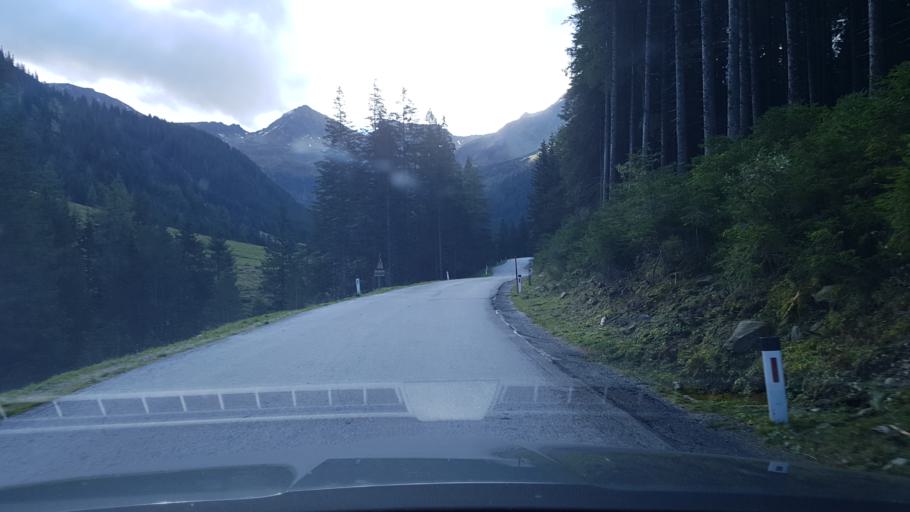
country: AT
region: Styria
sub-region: Politischer Bezirk Liezen
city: Sankt Nikolai im Solktal
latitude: 47.2934
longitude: 14.0762
